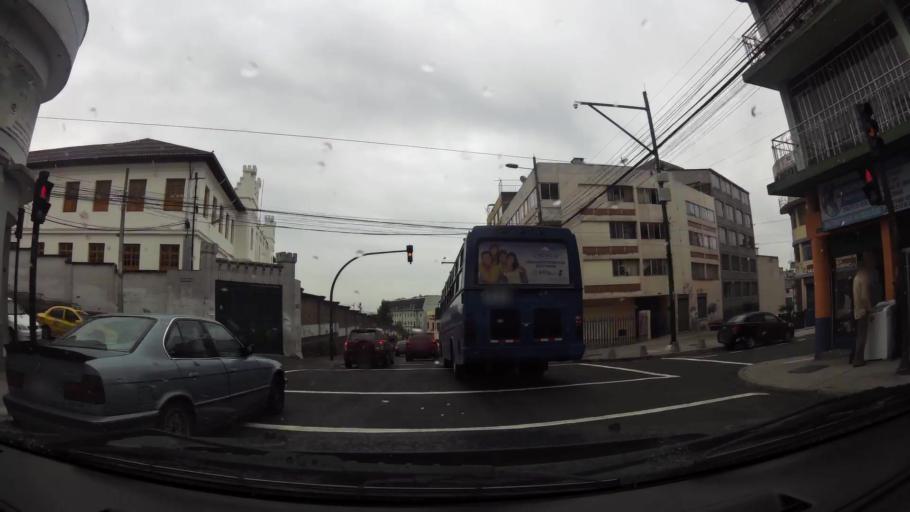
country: EC
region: Pichincha
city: Quito
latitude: -0.2142
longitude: -78.5055
